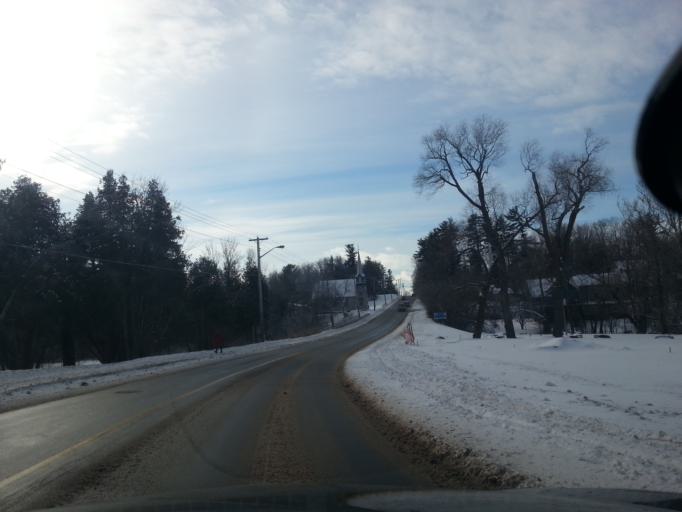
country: CA
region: Ontario
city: Carleton Place
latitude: 45.2242
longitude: -76.1988
